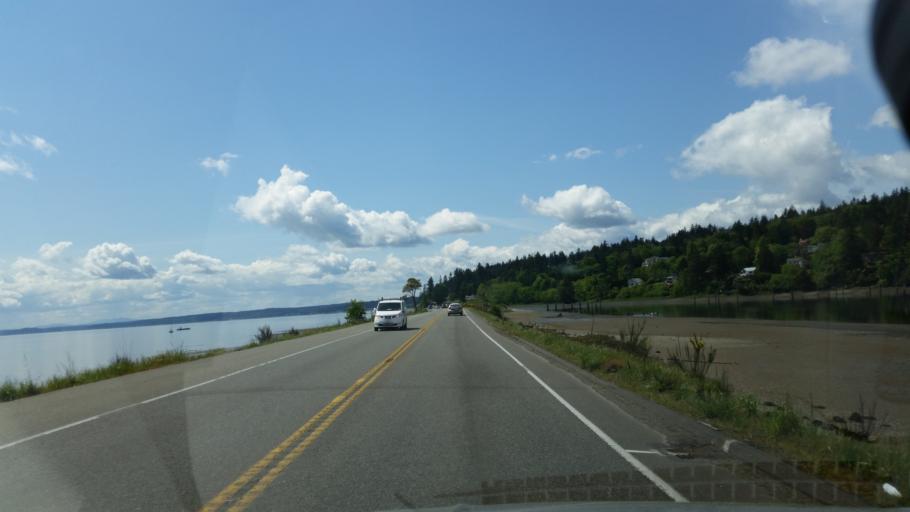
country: US
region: Washington
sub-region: Pierce County
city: Purdy
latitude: 47.3828
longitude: -122.6317
